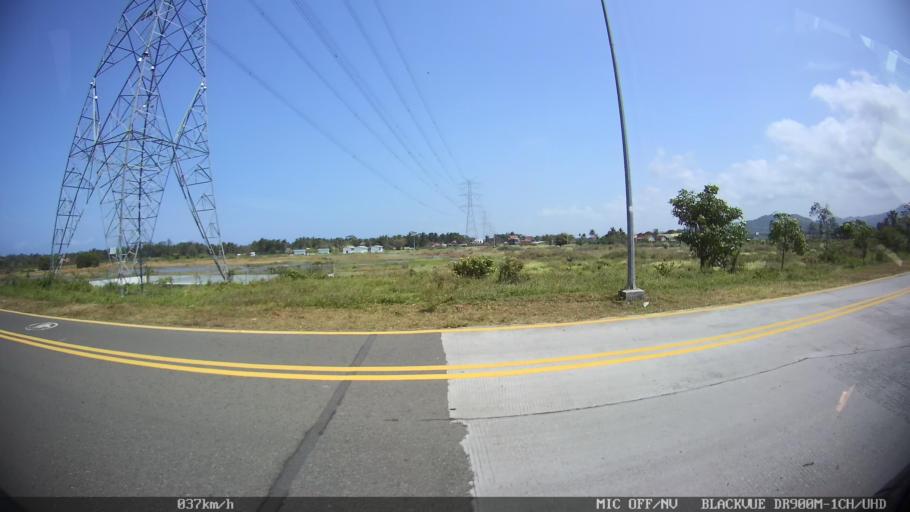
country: ID
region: Daerah Istimewa Yogyakarta
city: Srandakan
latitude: -7.8893
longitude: 110.0622
